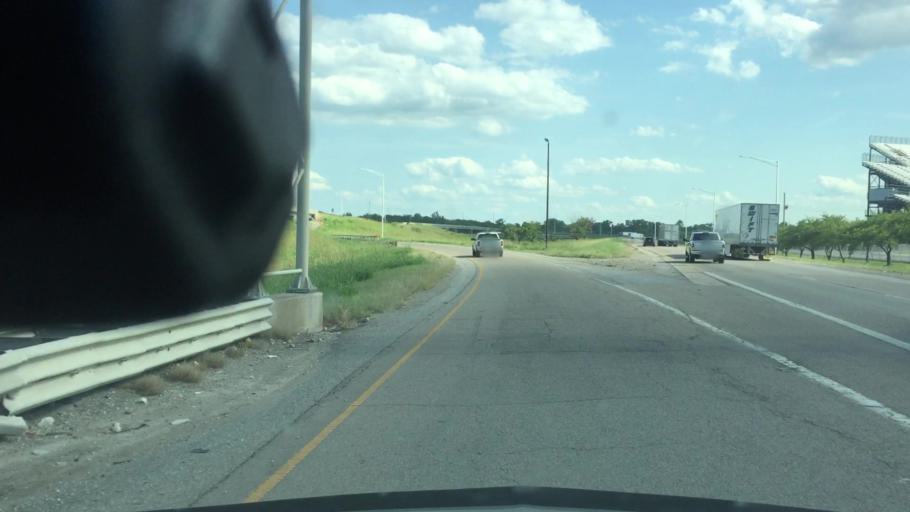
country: US
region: Illinois
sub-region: Saint Clair County
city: East Saint Louis
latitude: 38.6495
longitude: -90.1327
